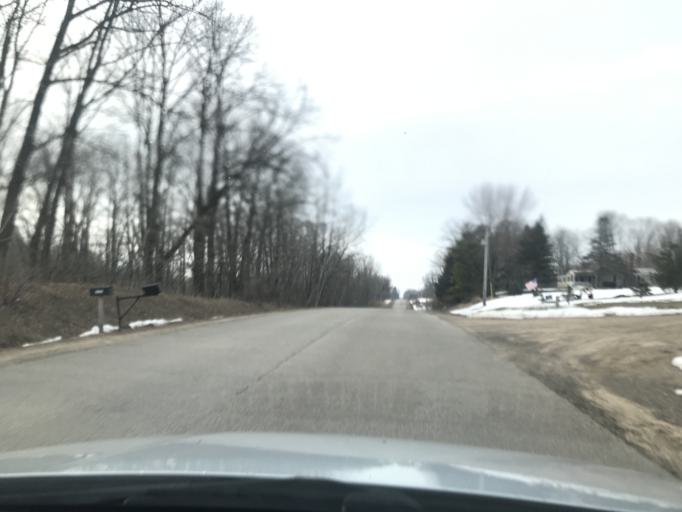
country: US
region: Wisconsin
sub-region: Oconto County
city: Oconto Falls
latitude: 44.8630
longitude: -88.1467
